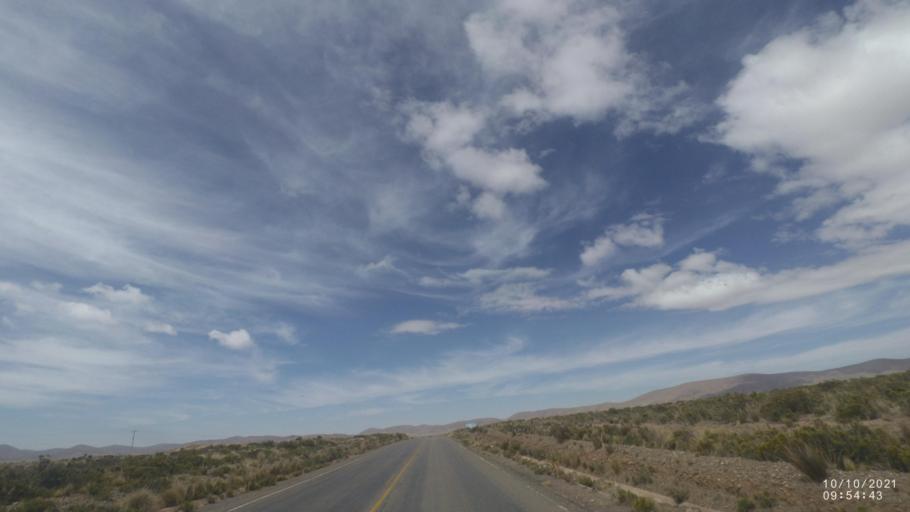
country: BO
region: La Paz
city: Colquiri
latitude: -17.2967
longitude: -67.3606
